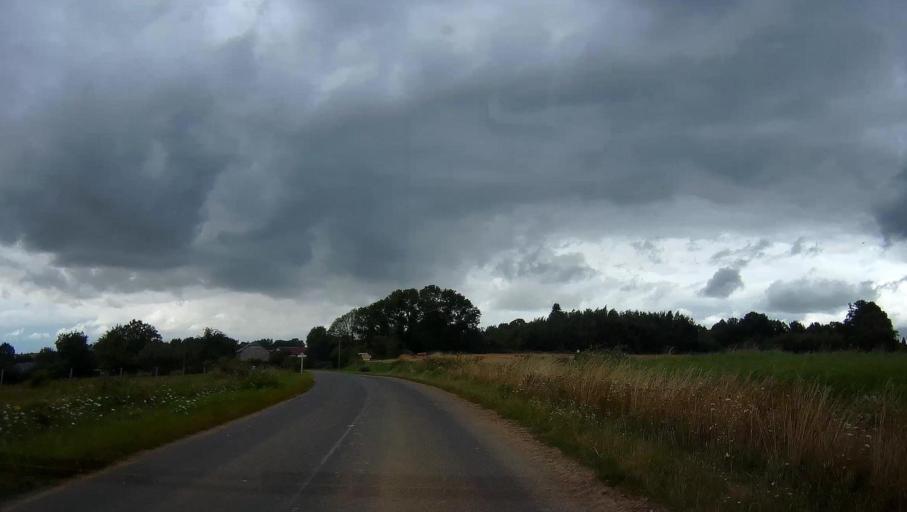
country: FR
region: Picardie
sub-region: Departement de l'Aisne
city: Rozoy-sur-Serre
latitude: 49.7064
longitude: 4.2271
